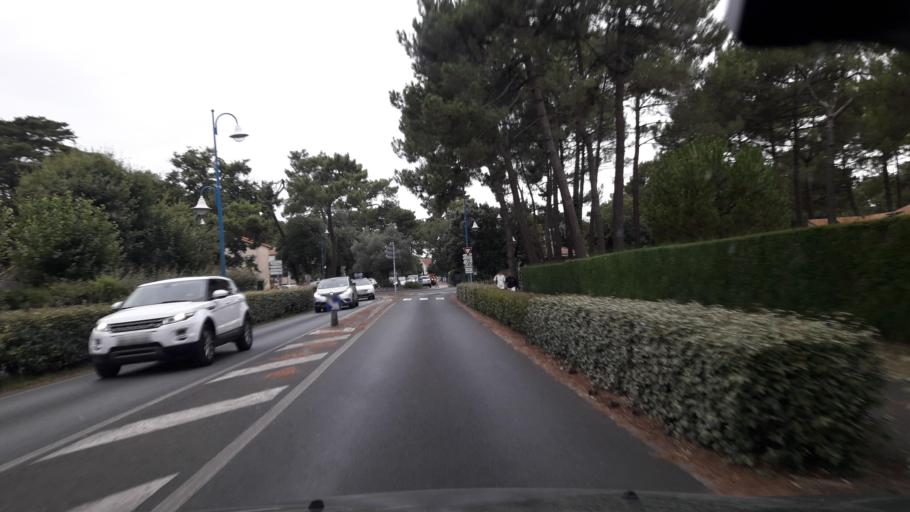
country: FR
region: Poitou-Charentes
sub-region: Departement de la Charente-Maritime
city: Les Mathes
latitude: 45.6946
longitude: -1.1771
